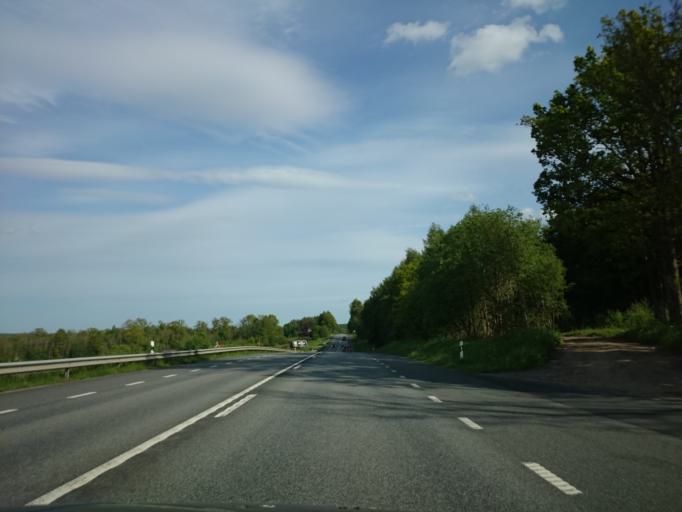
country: SE
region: Skane
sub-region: Kristianstads Kommun
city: Onnestad
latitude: 55.9364
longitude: 13.9140
